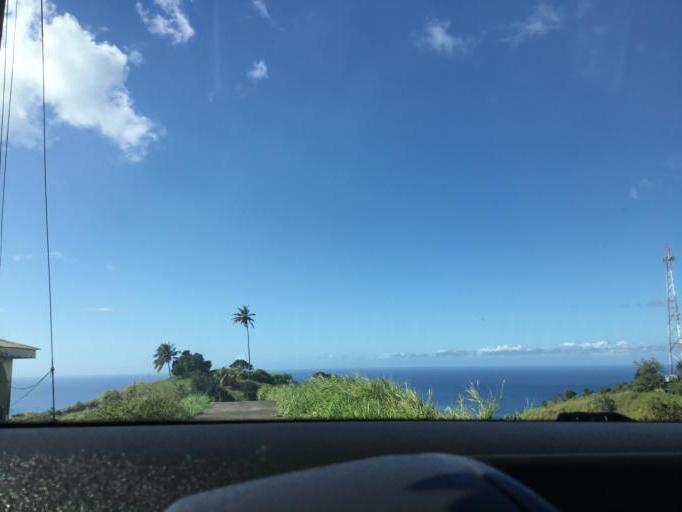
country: VC
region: Saint David
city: Chateaubelair
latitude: 13.2705
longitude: -61.2422
